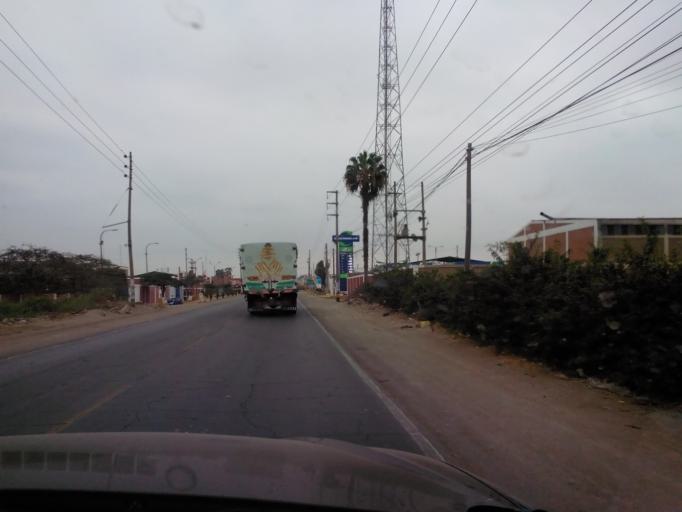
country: PE
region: Ica
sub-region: Provincia de Chincha
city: Chincha Baja
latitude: -13.4532
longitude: -76.1363
